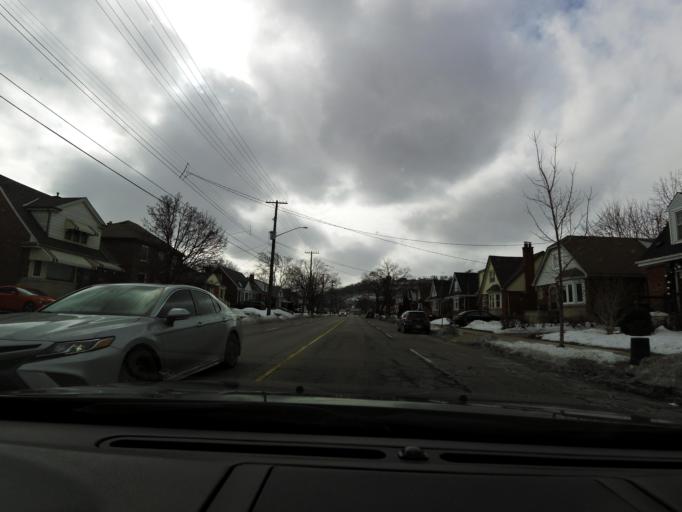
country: CA
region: Ontario
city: Hamilton
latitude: 43.2368
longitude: -79.8115
